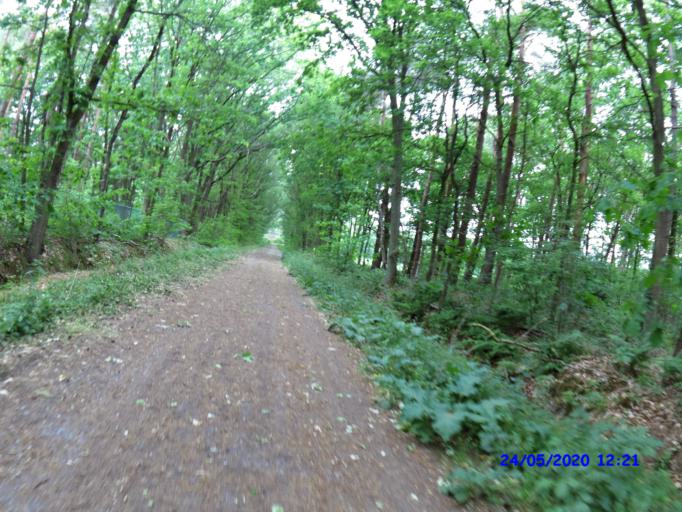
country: BE
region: Flanders
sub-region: Provincie Antwerpen
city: Mol
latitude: 51.1986
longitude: 5.0491
